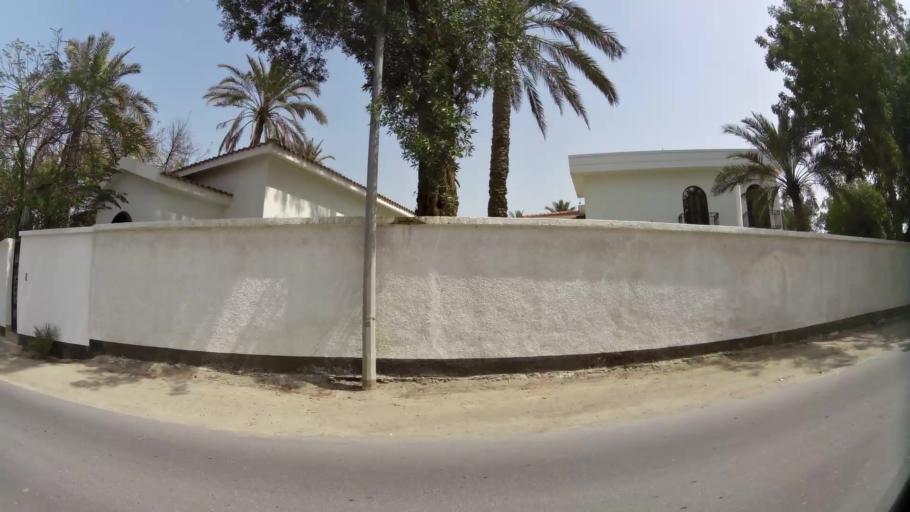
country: BH
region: Manama
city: Jidd Hafs
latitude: 26.2215
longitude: 50.4845
